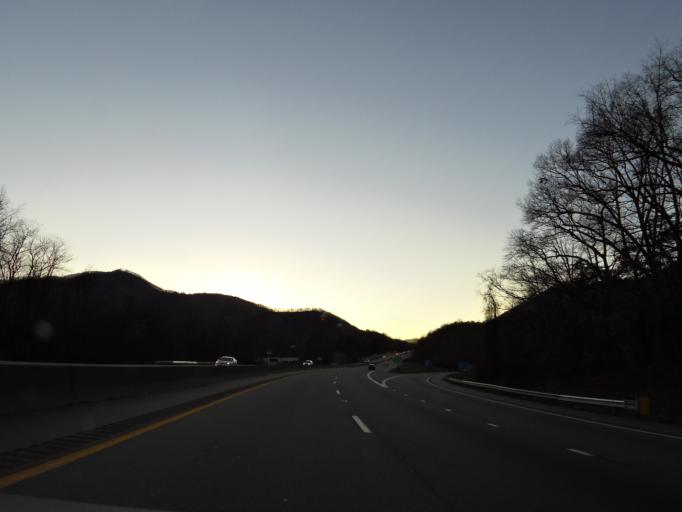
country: US
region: North Carolina
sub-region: Haywood County
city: Canton
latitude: 35.5428
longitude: -82.7493
